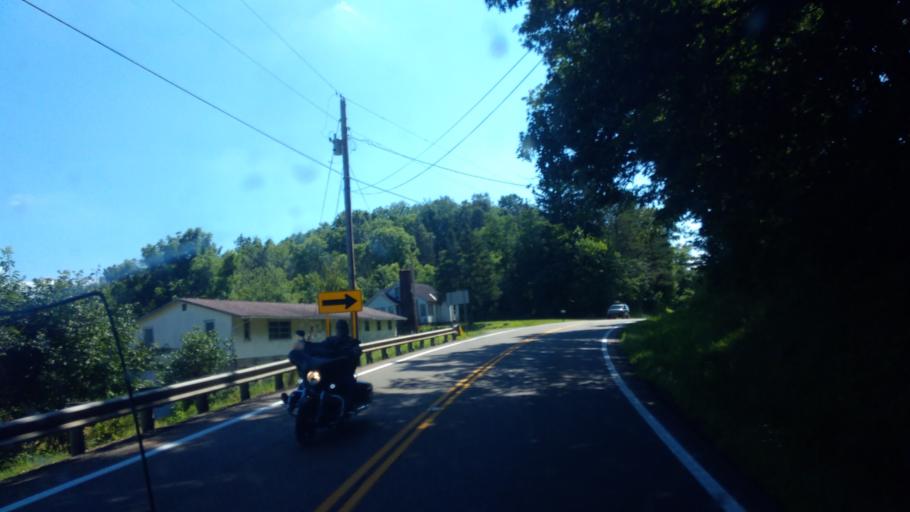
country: US
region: Ohio
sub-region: Carroll County
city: Carrollton
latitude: 40.5674
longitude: -81.1494
